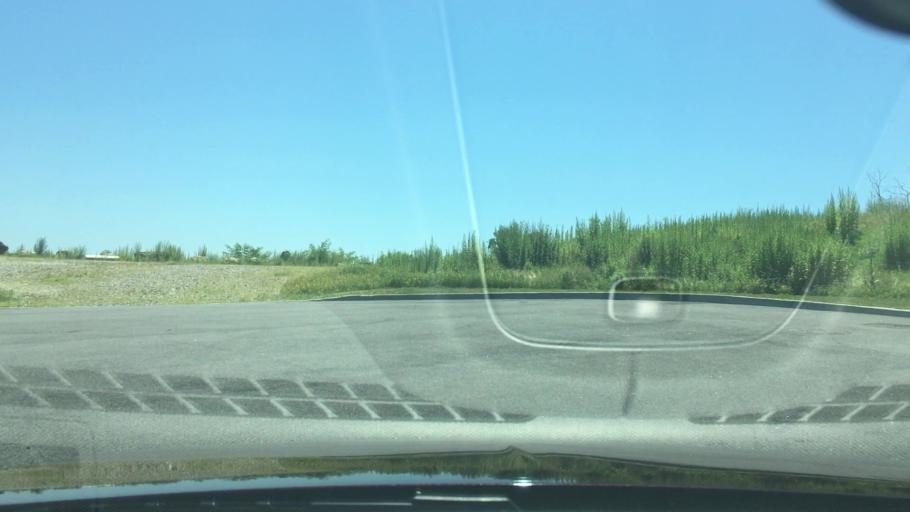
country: US
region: Connecticut
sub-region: New Haven County
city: Ansonia
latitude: 41.3554
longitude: -73.0958
